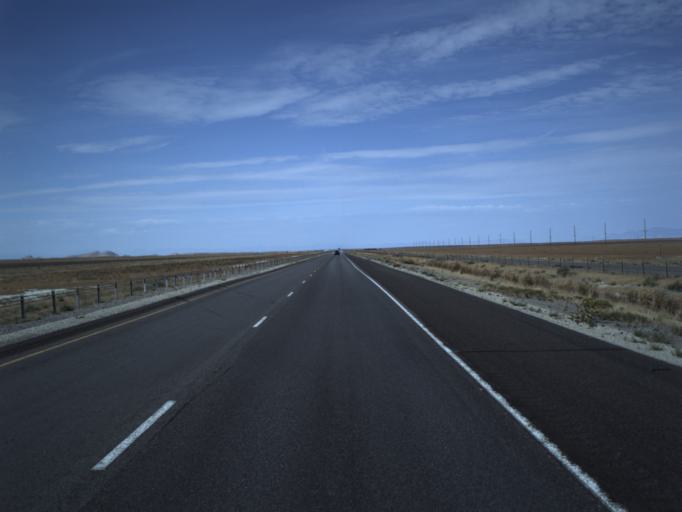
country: US
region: Utah
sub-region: Tooele County
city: Grantsville
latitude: 40.7263
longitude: -113.1725
